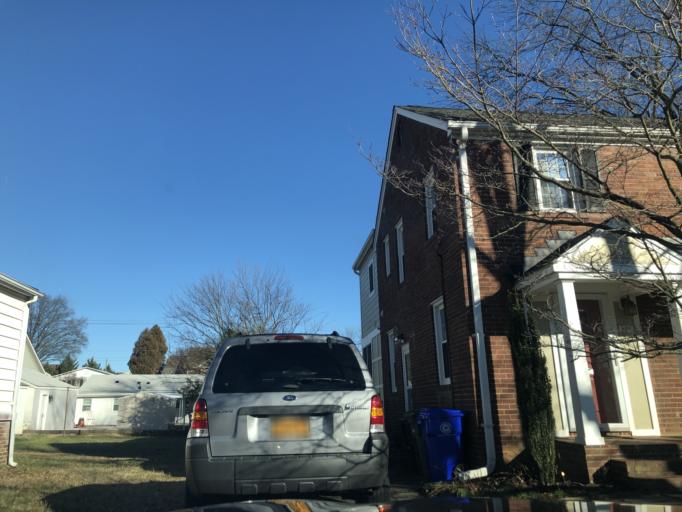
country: US
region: Virginia
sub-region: Arlington County
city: Arlington
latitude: 38.8763
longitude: -77.1249
